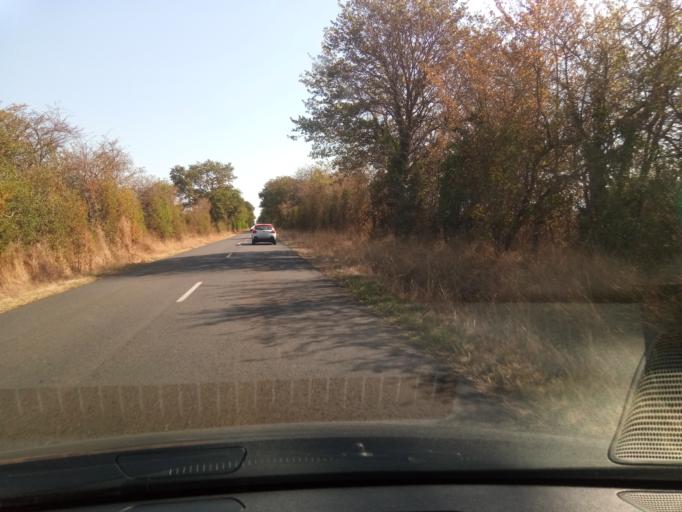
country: FR
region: Poitou-Charentes
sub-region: Departement de la Vienne
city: Montmorillon
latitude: 46.4362
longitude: 0.9182
